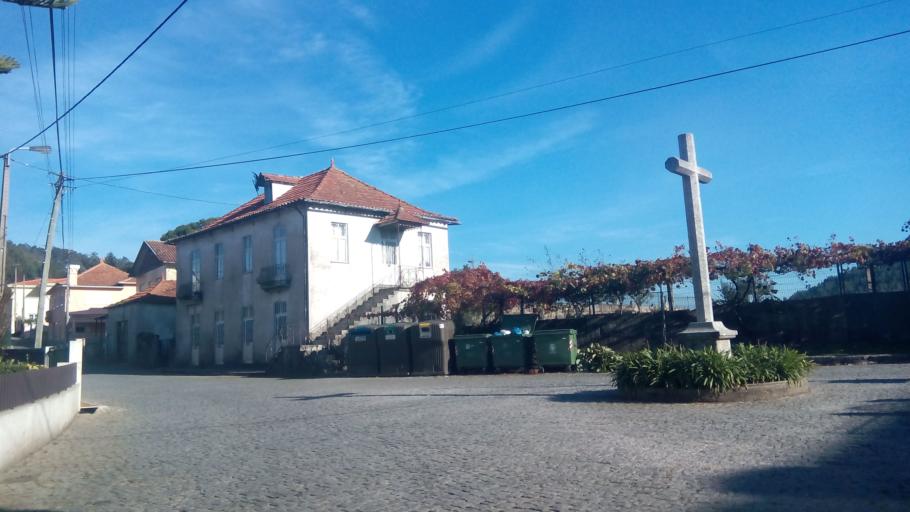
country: PT
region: Porto
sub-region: Paredes
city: Gandra
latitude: 41.1903
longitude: -8.4084
